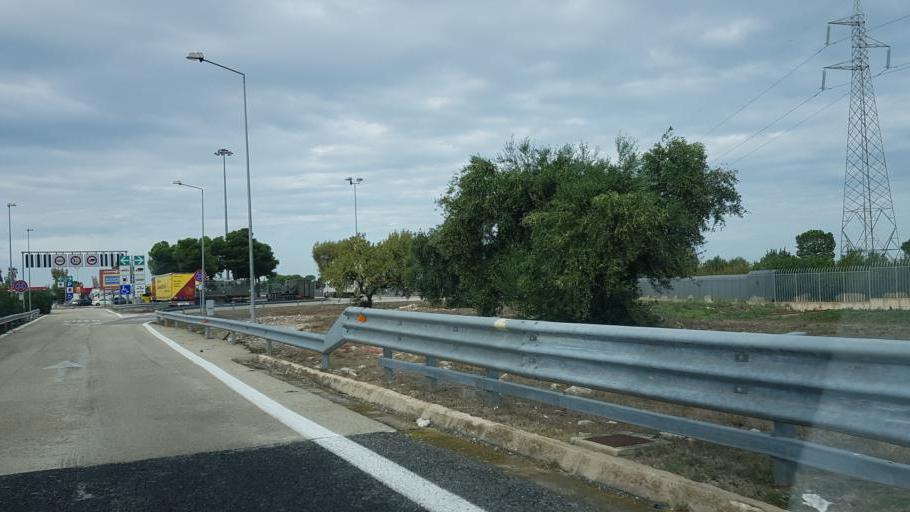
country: IT
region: Apulia
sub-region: Provincia di Barletta - Andria - Trani
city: Bisceglie
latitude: 41.1931
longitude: 16.4834
